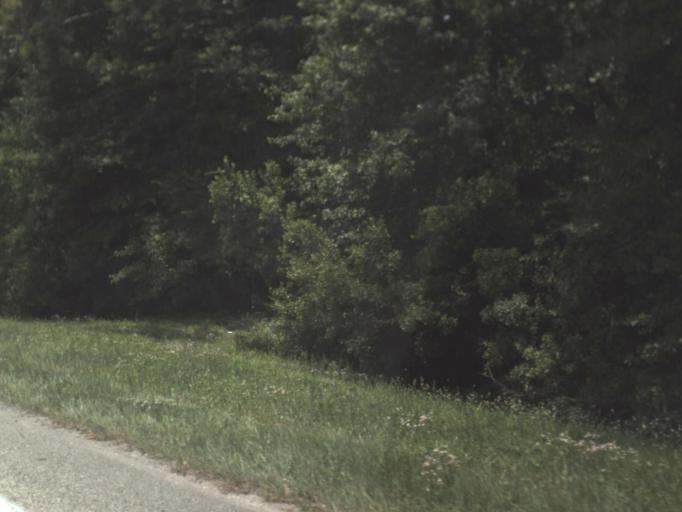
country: US
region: Florida
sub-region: Bradford County
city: Starke
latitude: 30.0688
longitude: -82.0663
